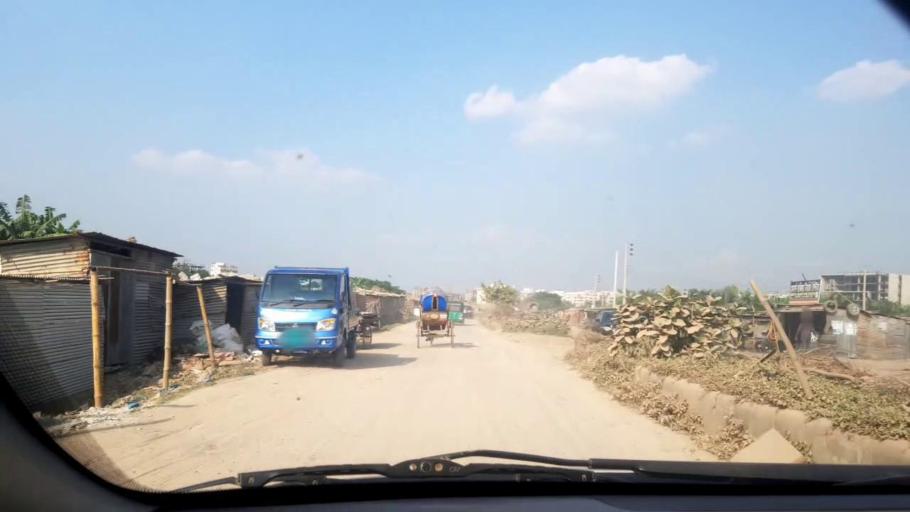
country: BD
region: Dhaka
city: Tungi
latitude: 23.8679
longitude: 90.3760
